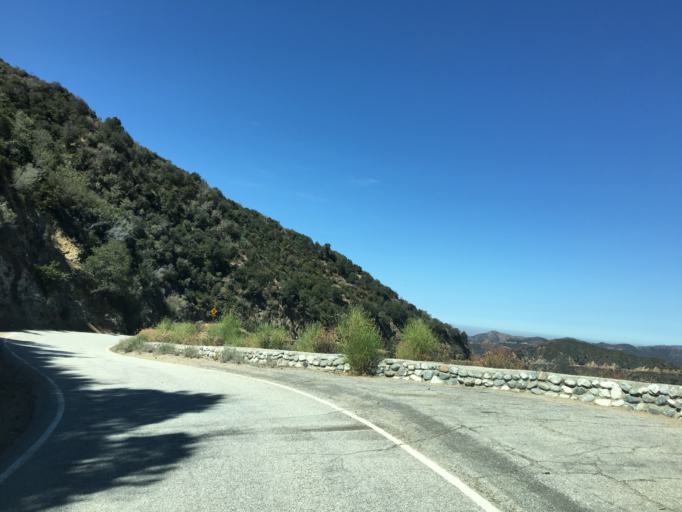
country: US
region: California
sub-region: San Bernardino County
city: San Antonio Heights
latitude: 34.2262
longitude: -117.7351
